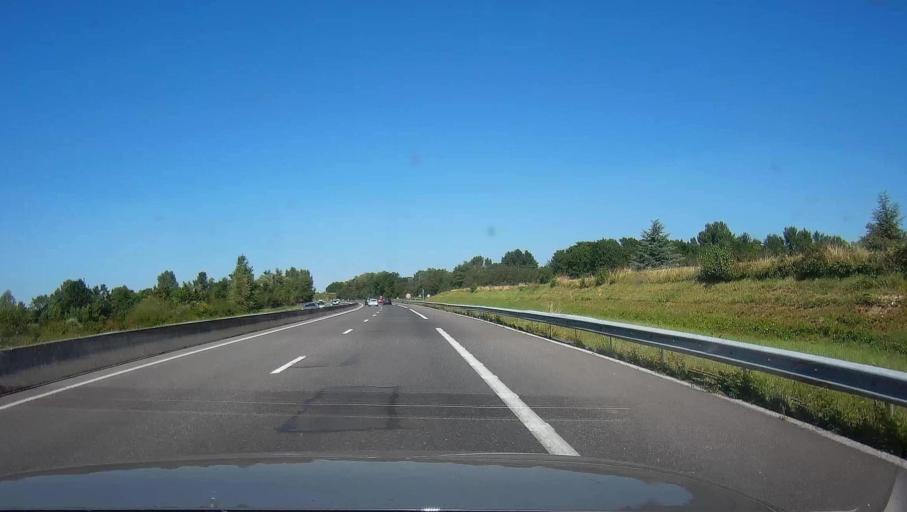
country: FR
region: Champagne-Ardenne
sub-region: Departement de la Marne
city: Fagnieres
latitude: 49.0074
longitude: 4.2983
